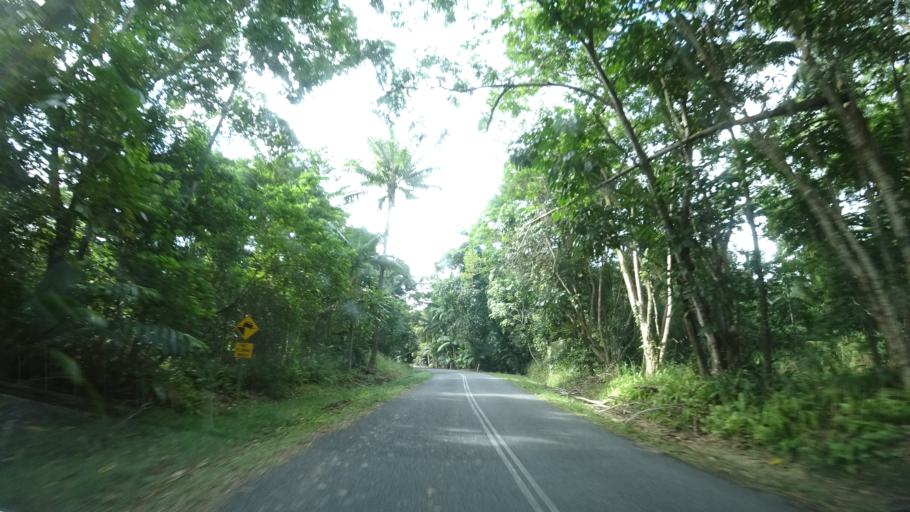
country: AU
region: Queensland
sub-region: Cairns
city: Port Douglas
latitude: -16.1024
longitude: 145.4581
